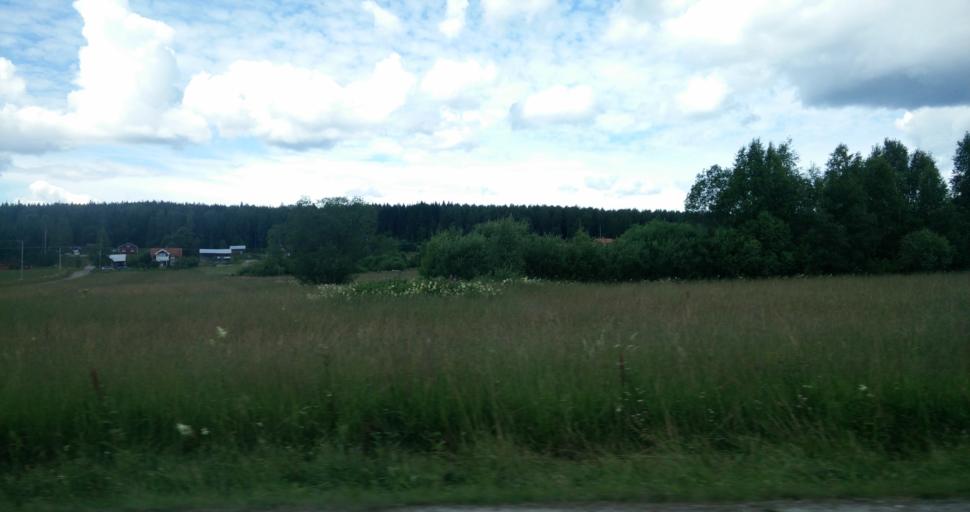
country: SE
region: Vaermland
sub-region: Hagfors Kommun
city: Ekshaerad
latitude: 60.1273
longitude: 13.4566
